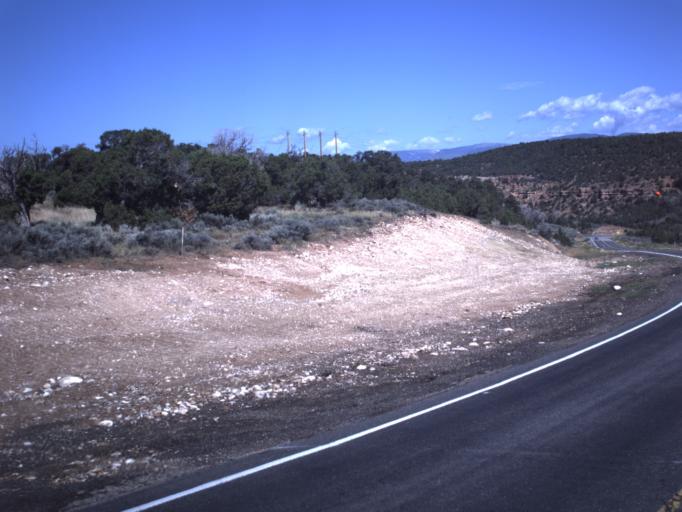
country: US
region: Utah
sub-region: Duchesne County
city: Duchesne
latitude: 40.3543
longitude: -110.3947
